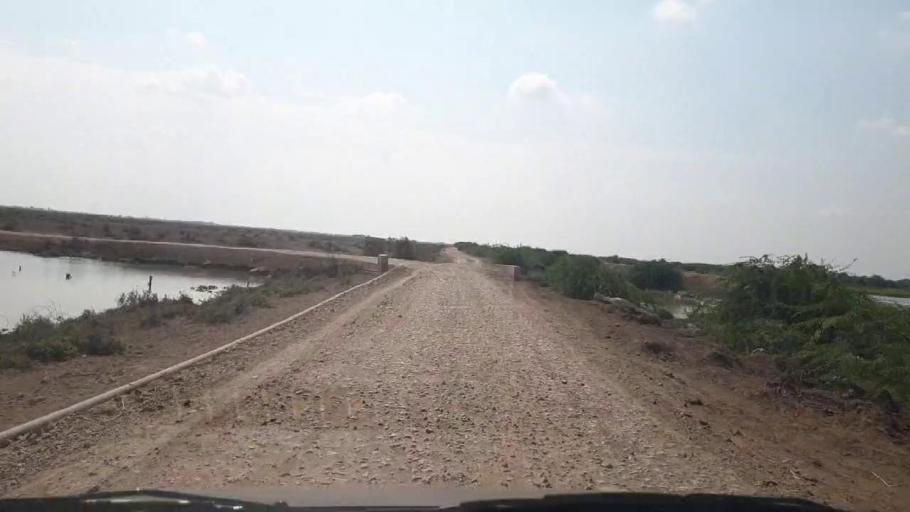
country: PK
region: Sindh
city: Badin
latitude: 24.5072
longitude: 68.6081
